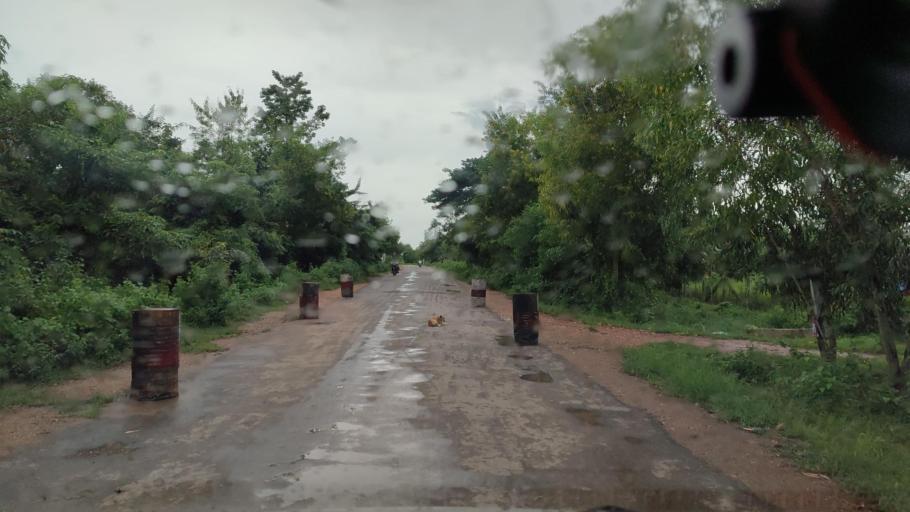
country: MM
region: Bago
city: Pyay
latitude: 18.7289
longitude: 95.3634
